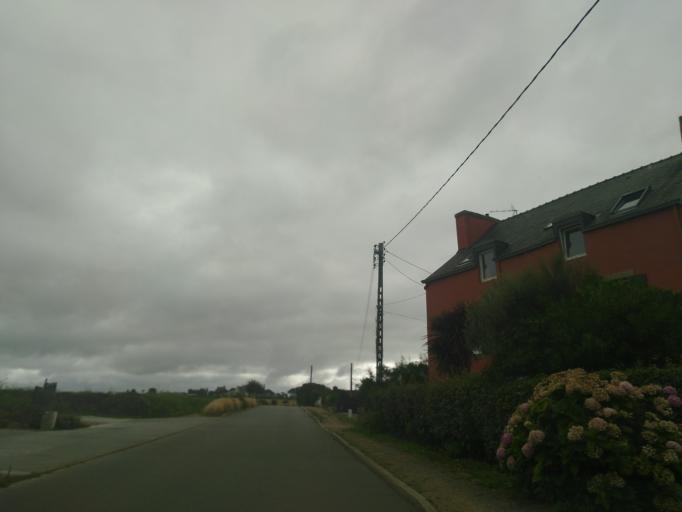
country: FR
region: Brittany
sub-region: Departement du Finistere
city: Plomodiern
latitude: 48.1739
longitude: -4.2881
